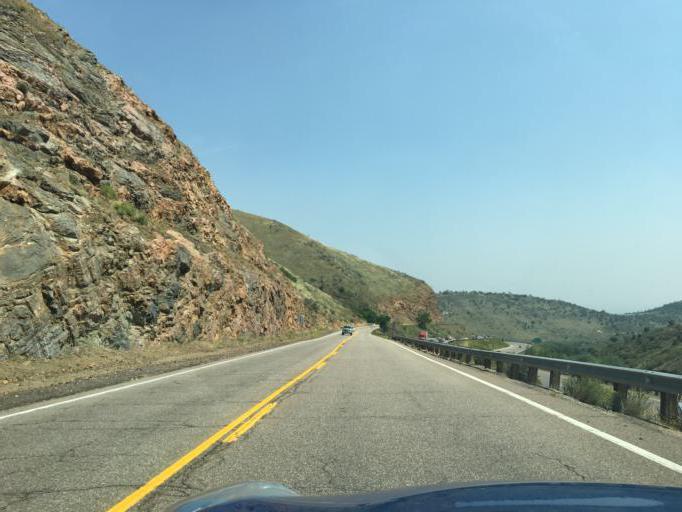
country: US
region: Colorado
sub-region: Jefferson County
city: West Pleasant View
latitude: 39.6964
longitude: -105.2177
